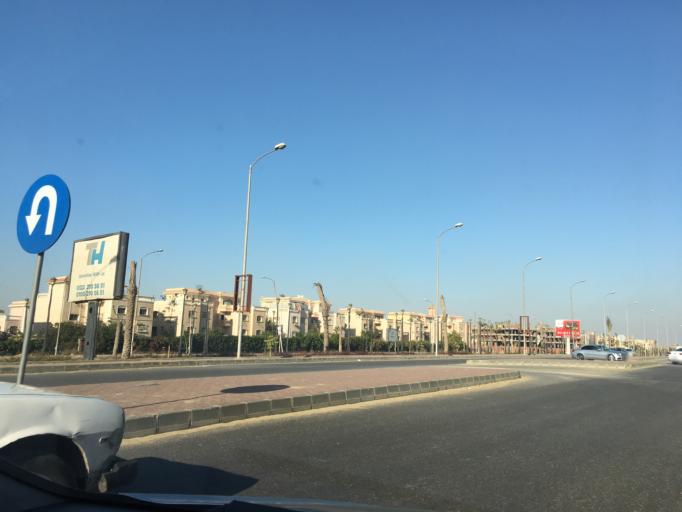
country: EG
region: Al Jizah
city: Madinat Sittah Uktubar
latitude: 30.0045
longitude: 30.9658
